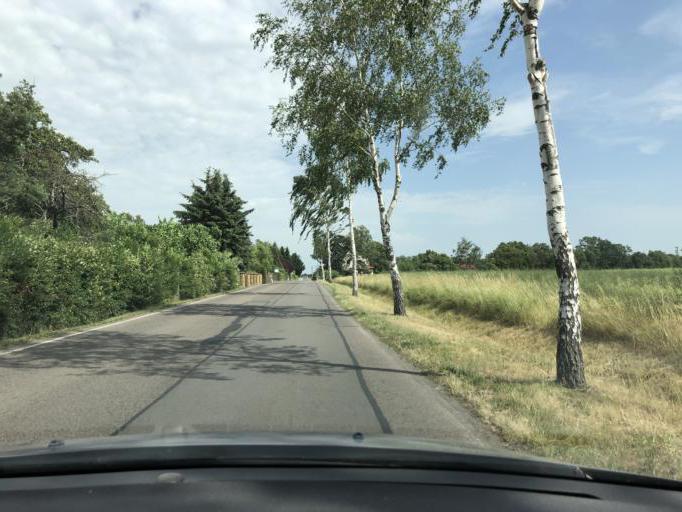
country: DE
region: Saxony
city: Borsdorf
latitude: 51.3696
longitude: 12.5112
